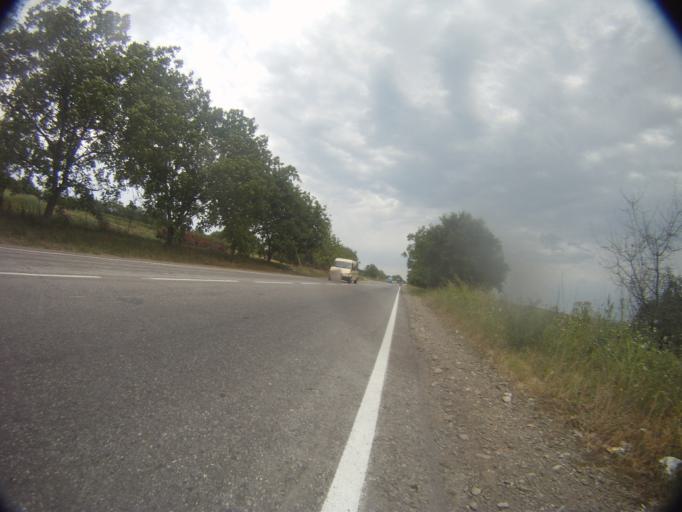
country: GE
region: Kakheti
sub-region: Gurjaani
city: Gurjaani
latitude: 41.6266
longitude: 45.7893
